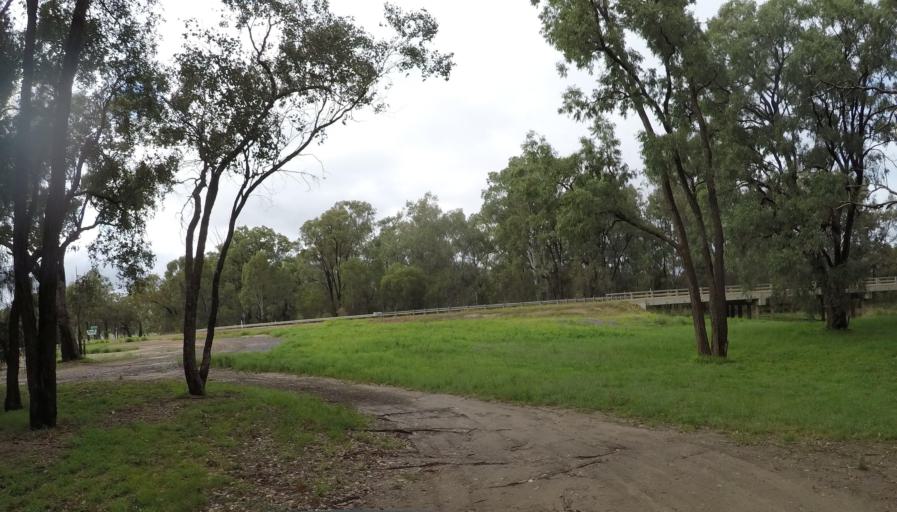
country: AU
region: Queensland
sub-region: Maranoa
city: Roma
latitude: -26.6110
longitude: 149.3898
